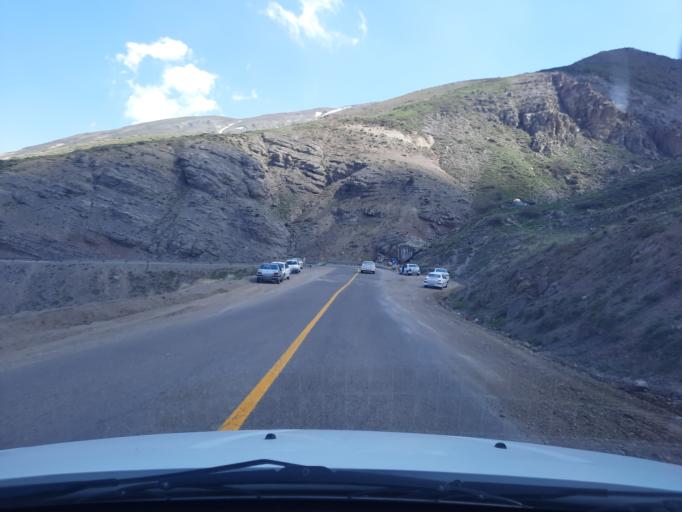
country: IR
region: Qazvin
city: Qazvin
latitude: 36.3982
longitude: 50.2171
